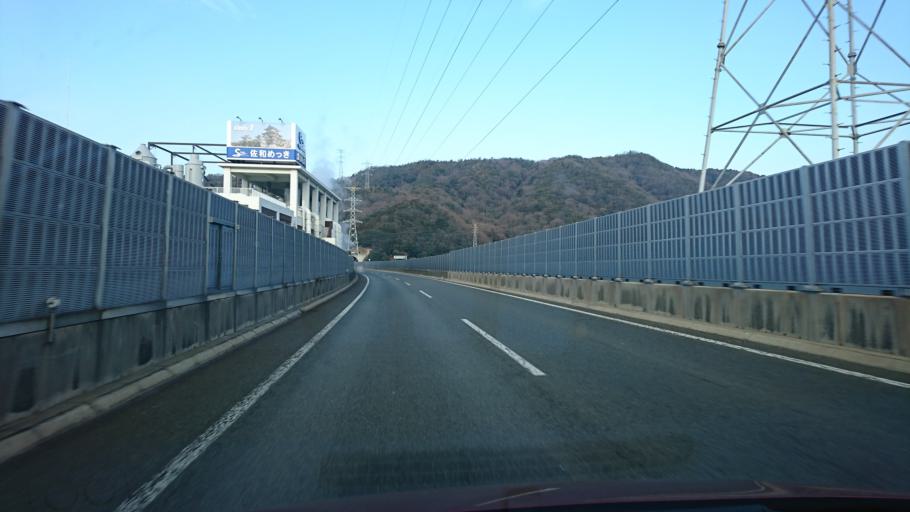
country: JP
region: Hyogo
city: Himeji
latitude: 34.8590
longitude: 134.7235
